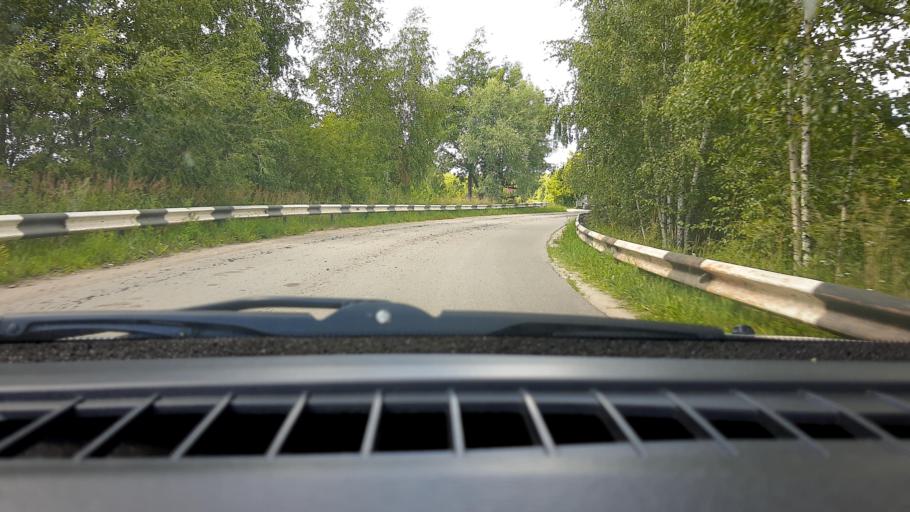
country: RU
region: Nizjnij Novgorod
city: Gorbatovka
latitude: 56.2221
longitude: 43.7551
